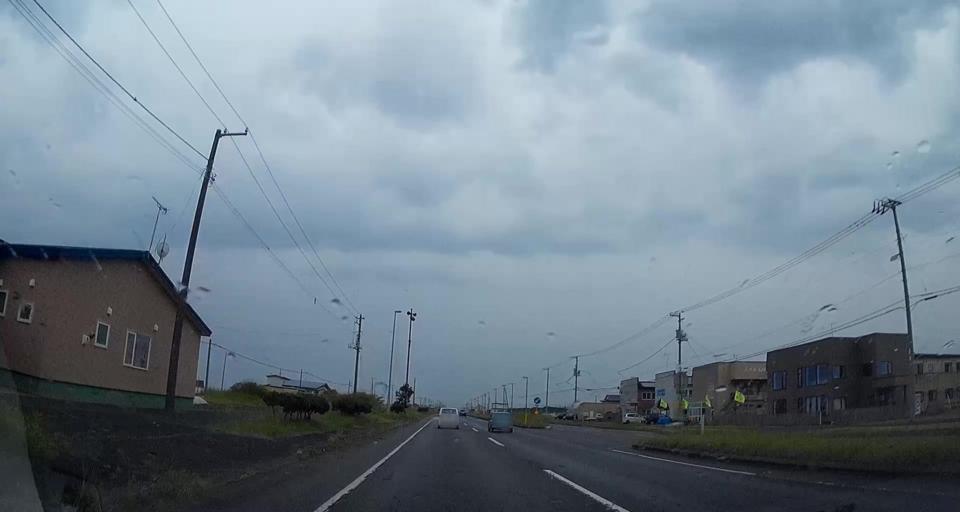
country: JP
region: Hokkaido
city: Tomakomai
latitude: 42.6027
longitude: 141.4907
